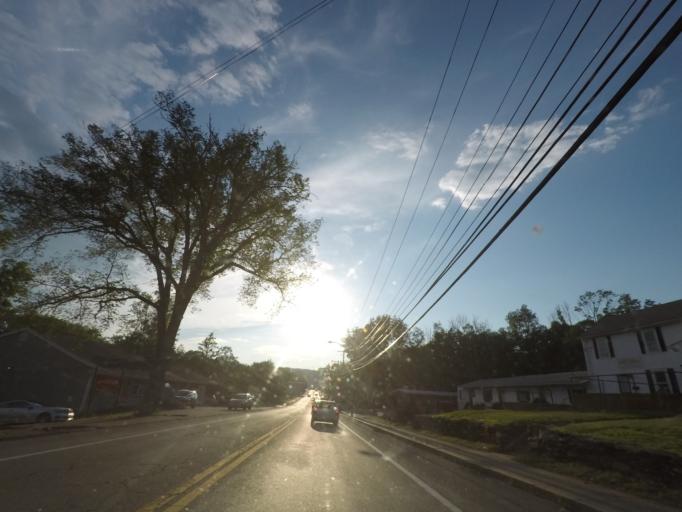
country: US
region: Massachusetts
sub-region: Worcester County
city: Fiskdale
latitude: 42.1145
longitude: -72.1066
